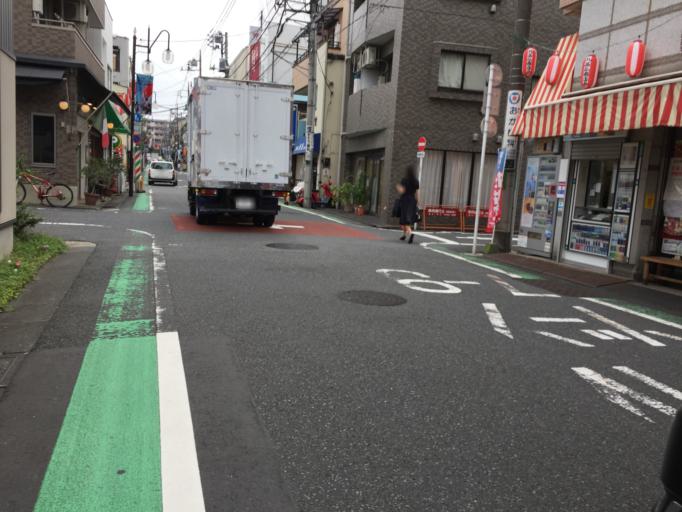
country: JP
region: Tokyo
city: Tokyo
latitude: 35.6040
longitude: 139.6611
